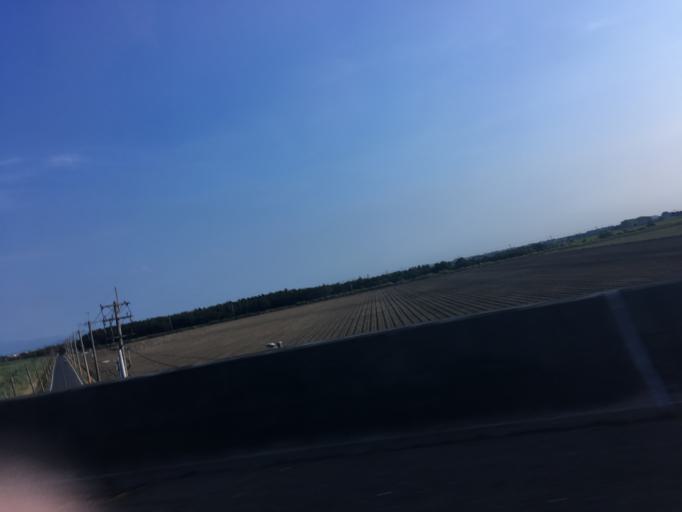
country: TW
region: Taiwan
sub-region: Chiayi
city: Taibao
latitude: 23.4268
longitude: 120.3460
